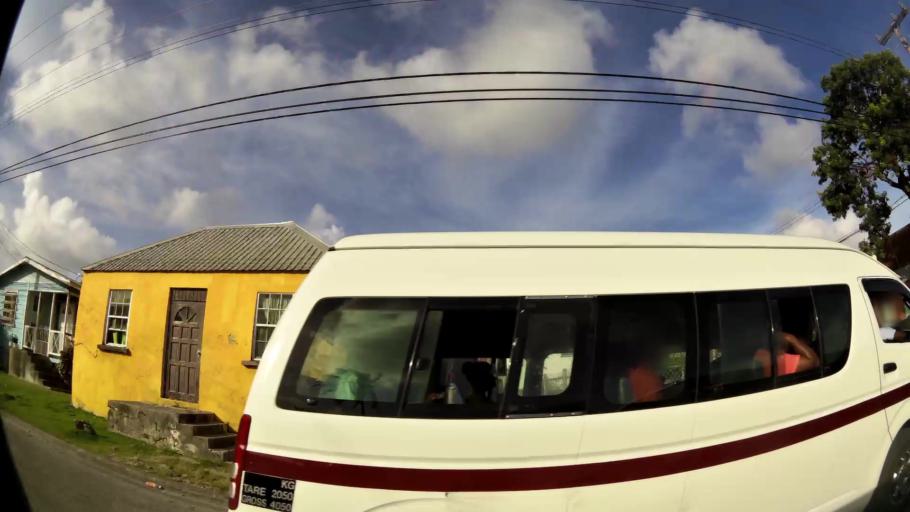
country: BB
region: Christ Church
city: Oistins
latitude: 13.0828
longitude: -59.5628
